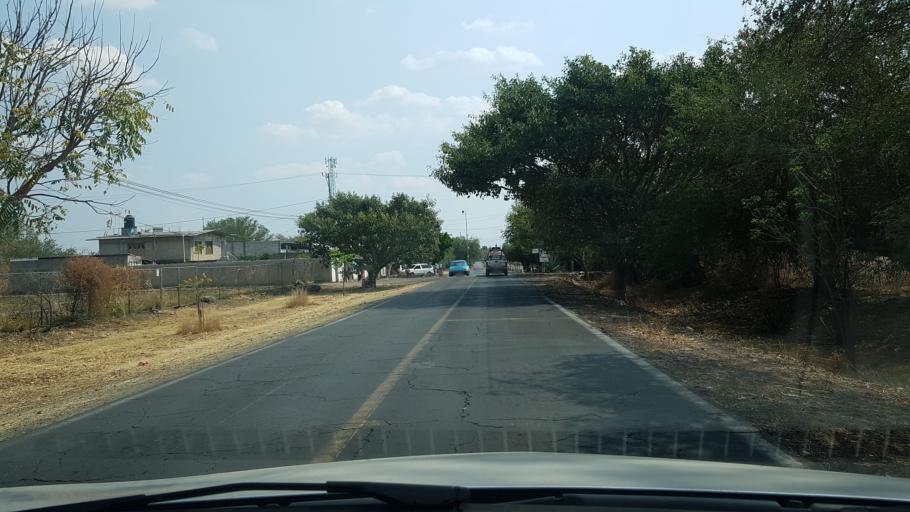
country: MX
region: Morelos
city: Amayuca
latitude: 18.7282
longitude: -98.7901
